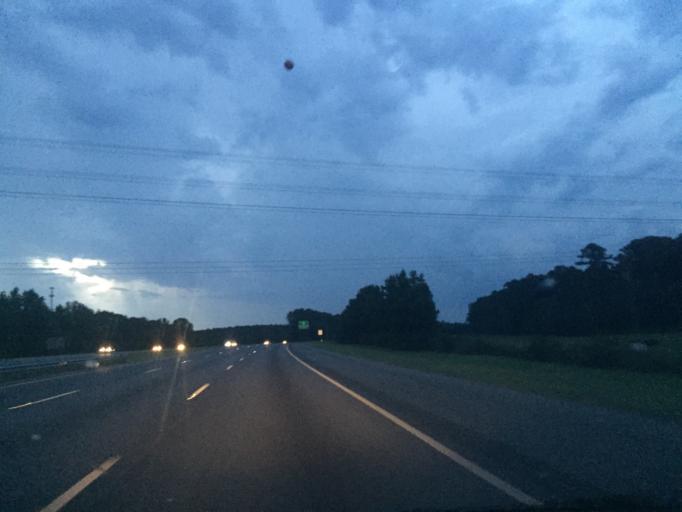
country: US
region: Georgia
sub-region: Bryan County
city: Richmond Hill
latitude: 31.9420
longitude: -81.3354
